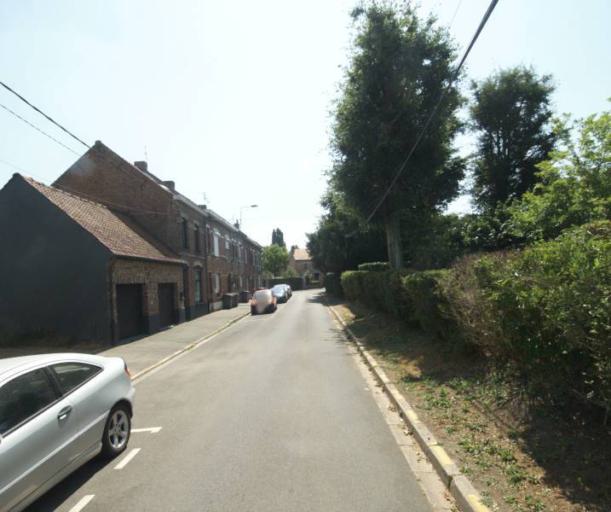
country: FR
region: Nord-Pas-de-Calais
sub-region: Departement du Nord
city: Roncq
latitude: 50.7357
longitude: 3.1238
